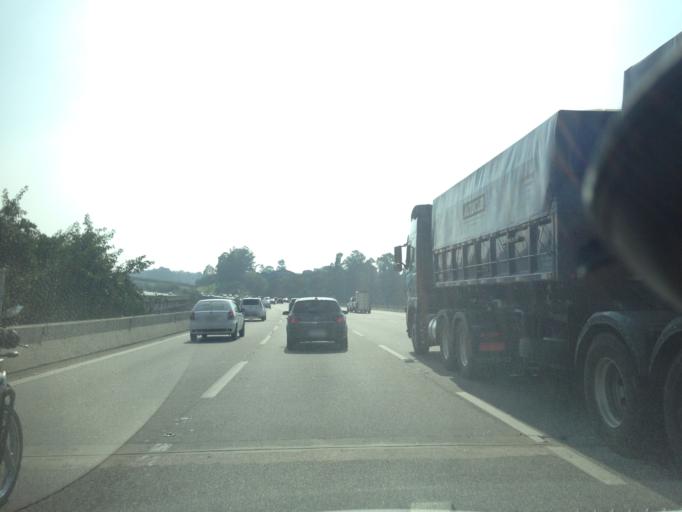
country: BR
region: Sao Paulo
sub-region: Diadema
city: Diadema
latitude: -23.6921
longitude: -46.6037
